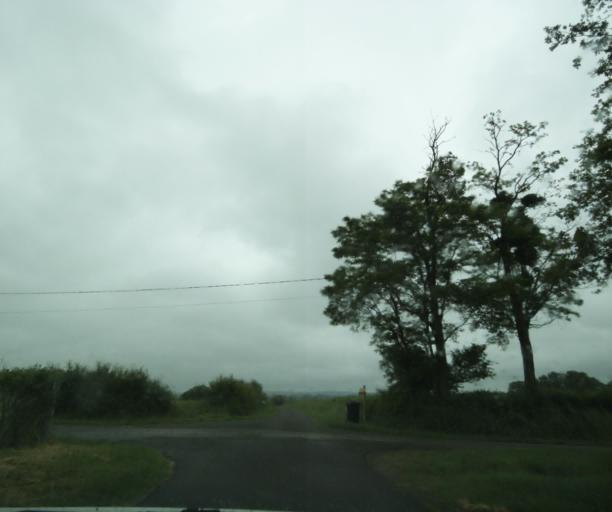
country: FR
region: Bourgogne
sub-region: Departement de Saone-et-Loire
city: Palinges
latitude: 46.5556
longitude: 4.1984
